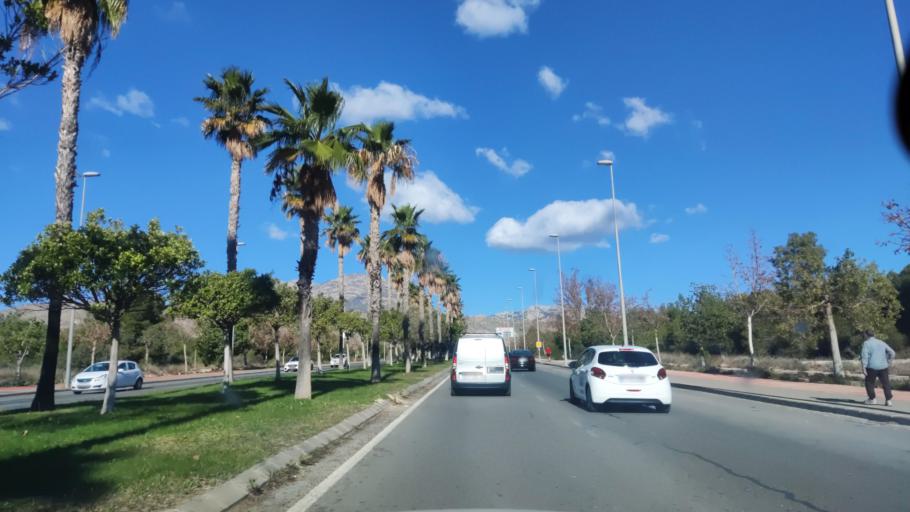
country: ES
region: Valencia
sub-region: Provincia de Alicante
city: Benidorm
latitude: 38.5388
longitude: -0.1587
